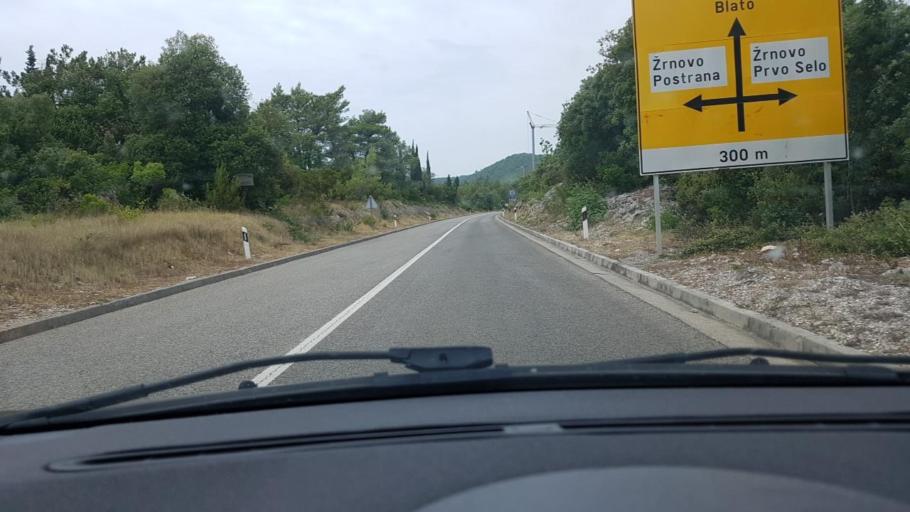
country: HR
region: Dubrovacko-Neretvanska
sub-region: Grad Korcula
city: Zrnovo
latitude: 42.9451
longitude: 17.1147
